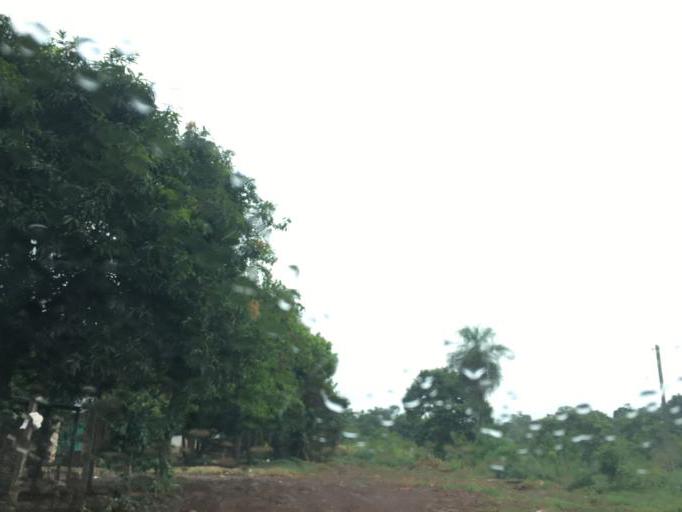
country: PY
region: Alto Parana
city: Ciudad del Este
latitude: -25.4355
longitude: -54.6545
